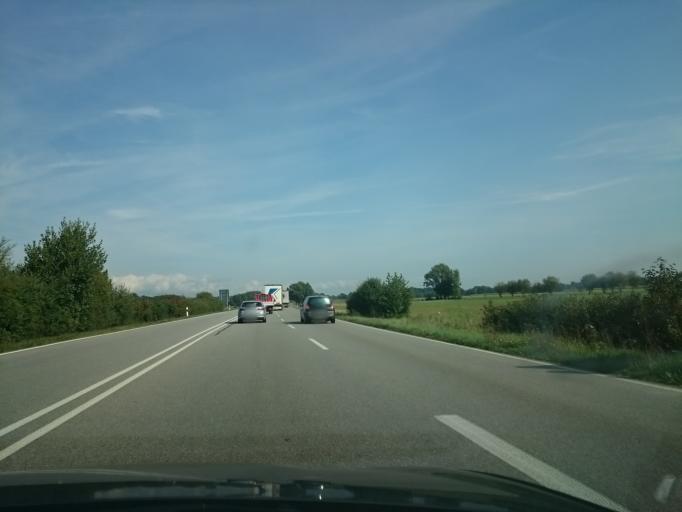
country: DE
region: Bavaria
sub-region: Upper Bavaria
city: Pornbach
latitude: 48.6254
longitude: 11.4433
